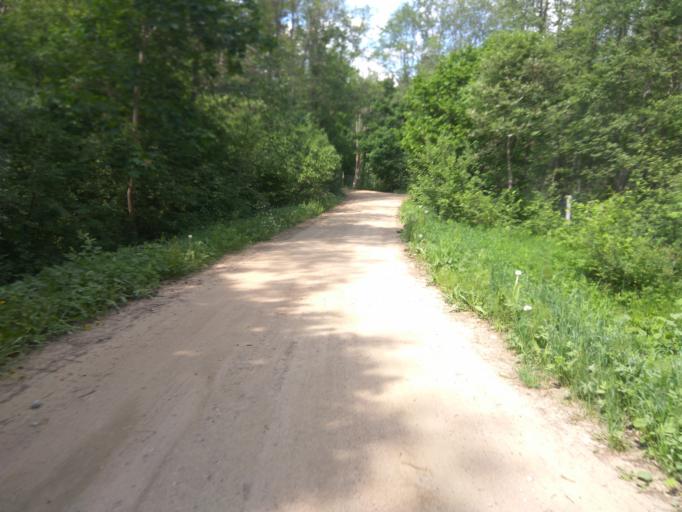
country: LV
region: Kuldigas Rajons
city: Kuldiga
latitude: 56.8855
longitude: 21.9273
